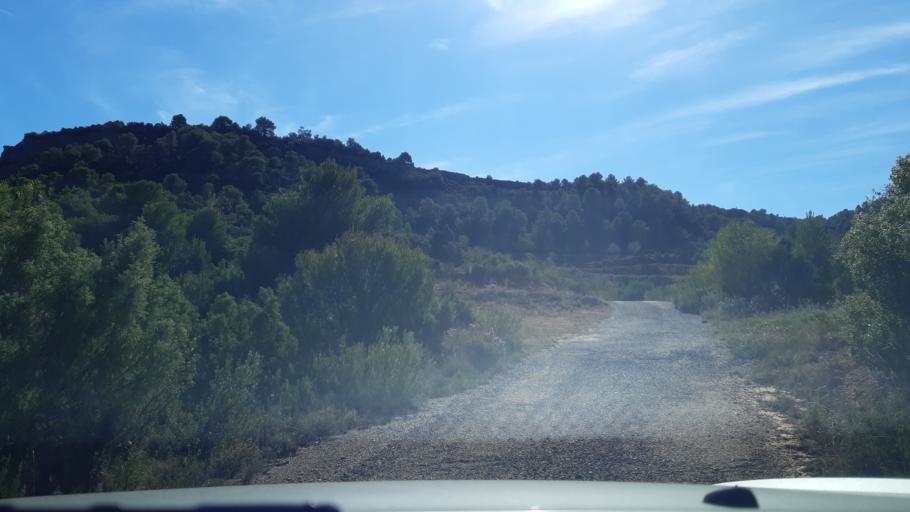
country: ES
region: Aragon
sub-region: Provincia de Teruel
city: Valderrobres
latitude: 40.8386
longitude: 0.2004
